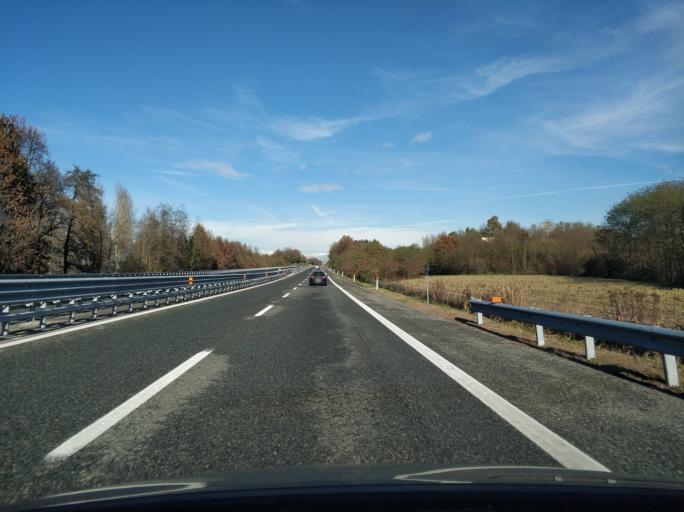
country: IT
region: Piedmont
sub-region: Provincia di Torino
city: San Giusto Canavese
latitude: 45.2966
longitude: 7.8162
